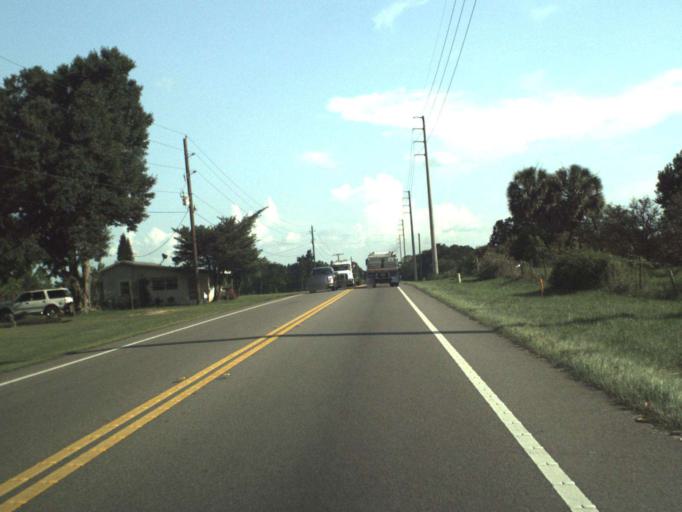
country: US
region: Florida
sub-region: Lake County
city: Groveland
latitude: 28.5451
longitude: -81.8516
